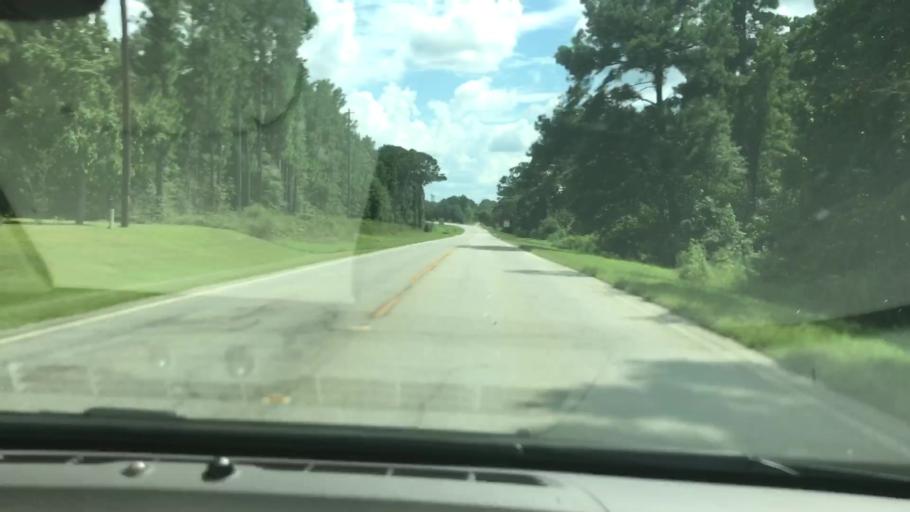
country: US
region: Georgia
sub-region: Clay County
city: Fort Gaines
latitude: 31.6571
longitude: -85.0474
